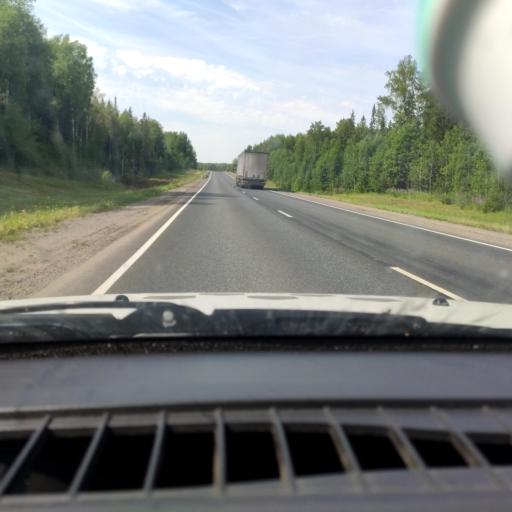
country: RU
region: Kirov
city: Kostino
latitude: 58.7195
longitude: 53.6698
